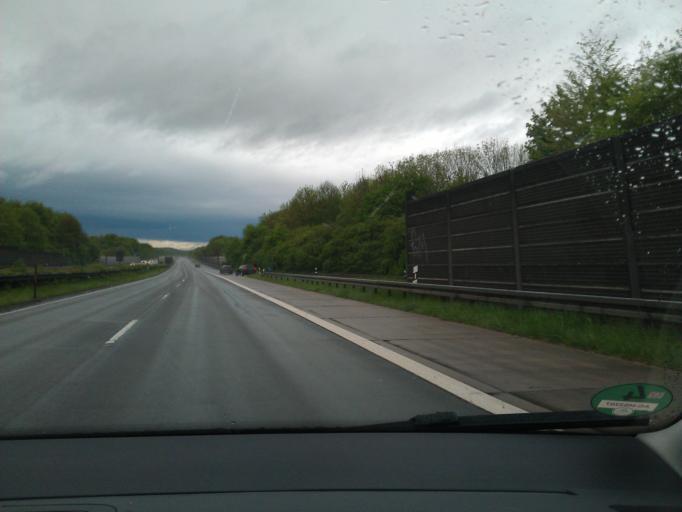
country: DE
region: North Rhine-Westphalia
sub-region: Regierungsbezirk Koln
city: Hennef
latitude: 50.7753
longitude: 7.3017
